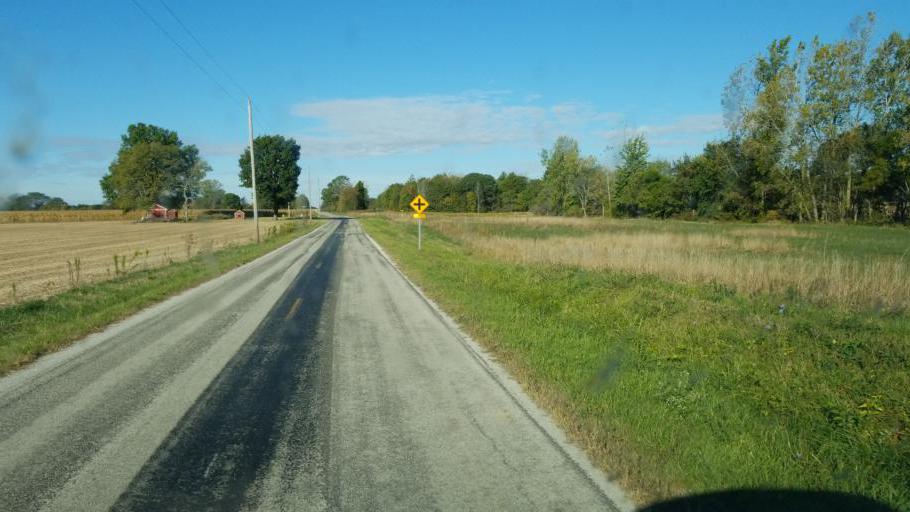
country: US
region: Ohio
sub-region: Crawford County
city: Bucyrus
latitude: 40.6896
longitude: -82.9366
